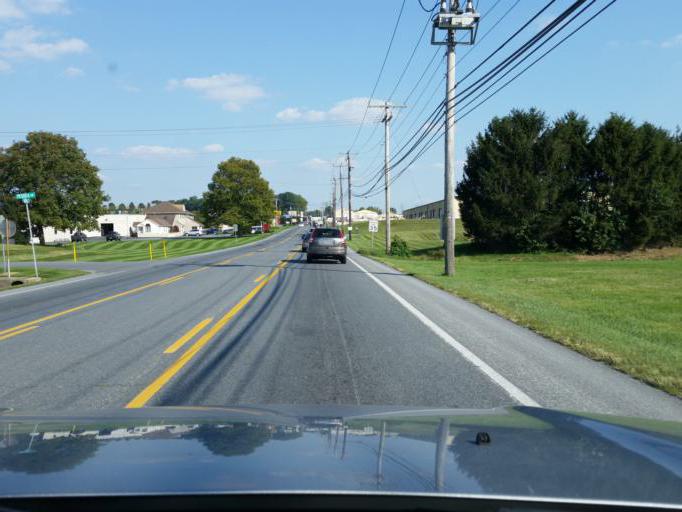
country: US
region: Pennsylvania
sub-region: Lancaster County
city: Paradise
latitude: 40.0044
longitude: -76.1027
